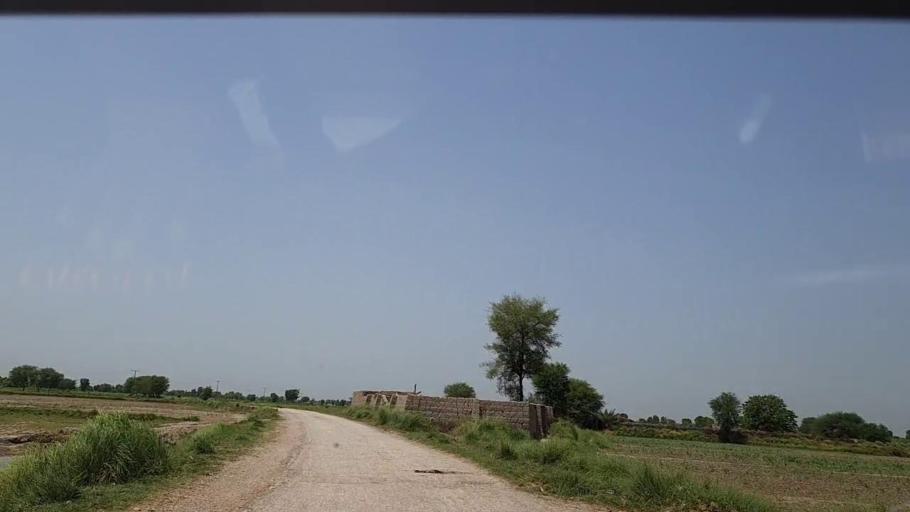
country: PK
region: Sindh
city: Tharu Shah
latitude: 26.9260
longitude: 68.0557
